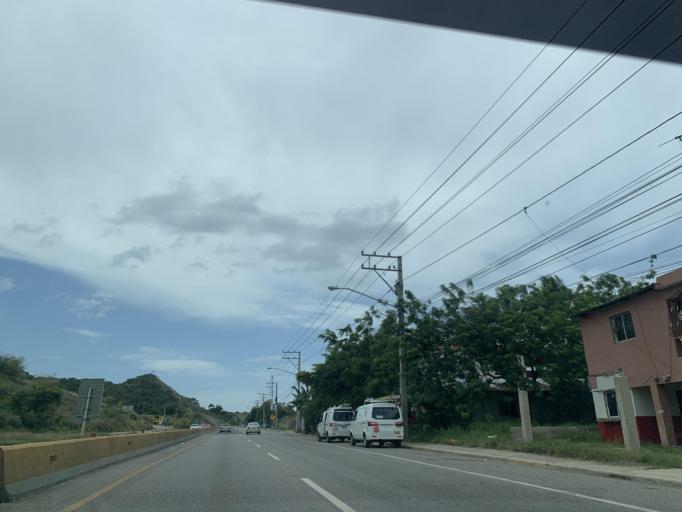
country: DO
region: Puerto Plata
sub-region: Puerto Plata
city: Puerto Plata
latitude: 19.8233
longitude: -70.7432
